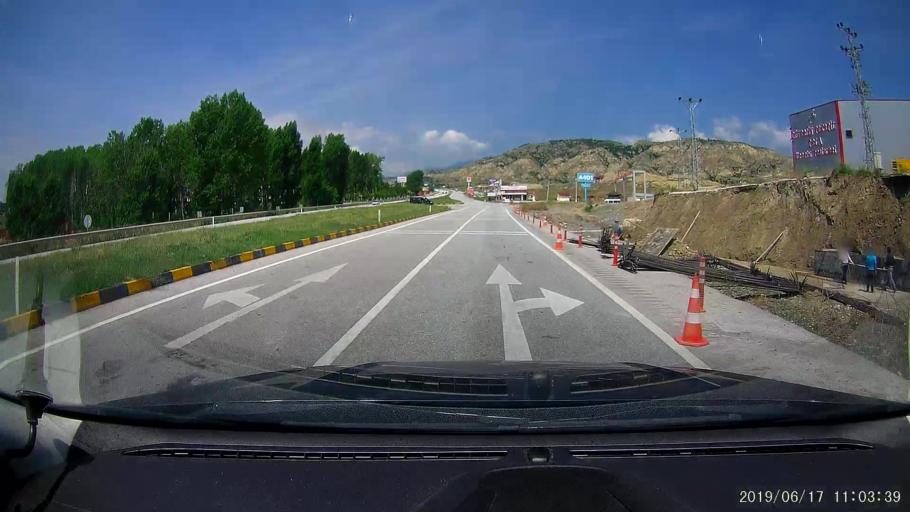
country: TR
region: Kastamonu
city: Tosya
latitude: 41.0186
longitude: 34.1120
